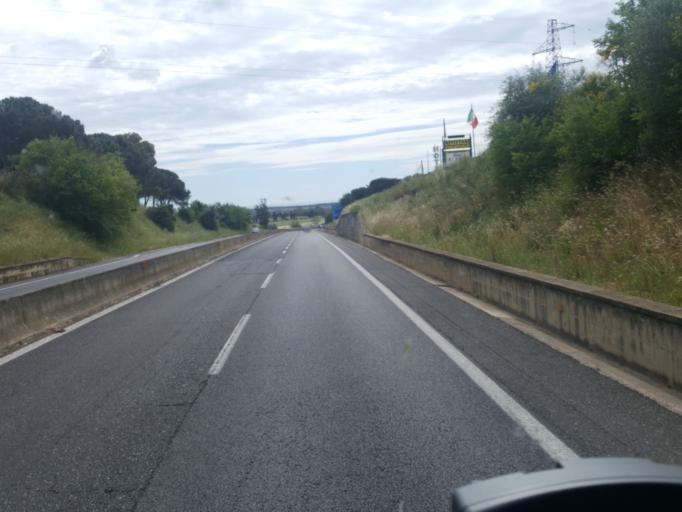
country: IT
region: Latium
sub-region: Citta metropolitana di Roma Capitale
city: Ara Nova
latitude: 41.9171
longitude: 12.2286
